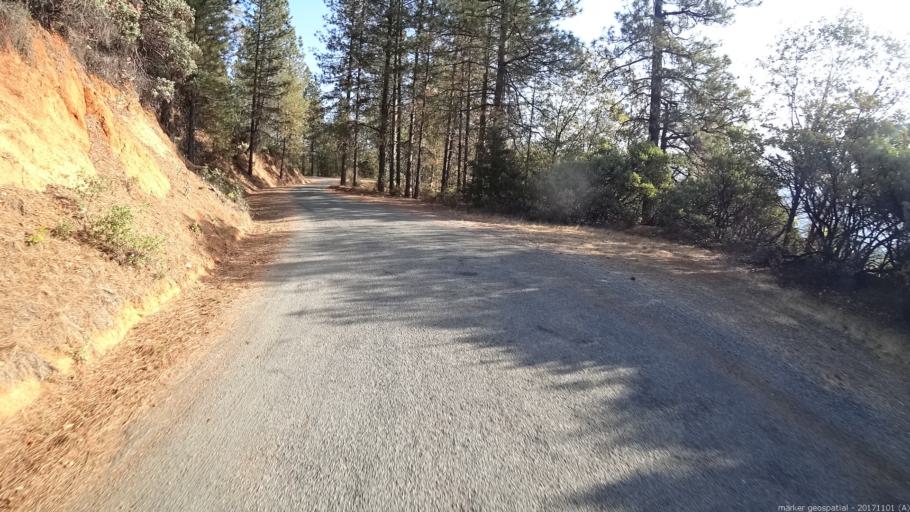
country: US
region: California
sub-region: Shasta County
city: Shasta Lake
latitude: 40.8095
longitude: -122.3110
